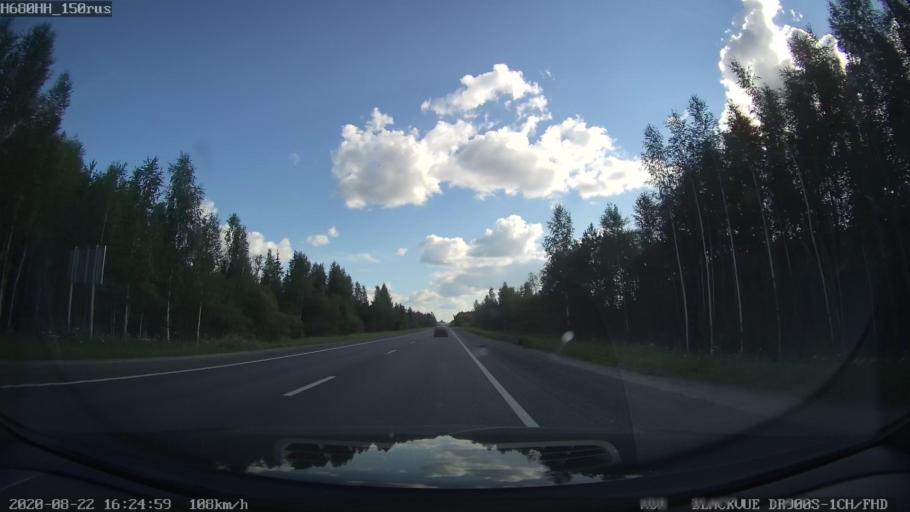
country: RU
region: Tverskaya
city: Rameshki
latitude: 57.3283
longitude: 36.0924
